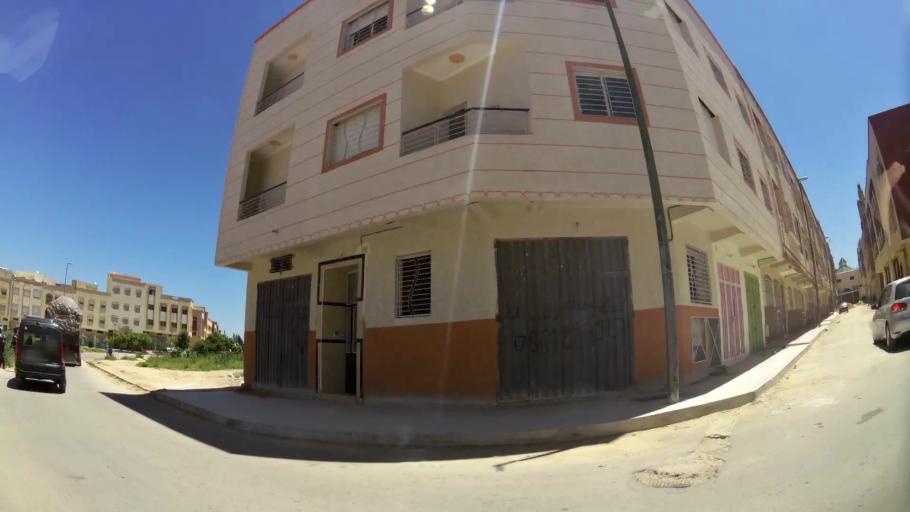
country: MA
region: Meknes-Tafilalet
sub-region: Meknes
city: Meknes
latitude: 33.8534
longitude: -5.5577
